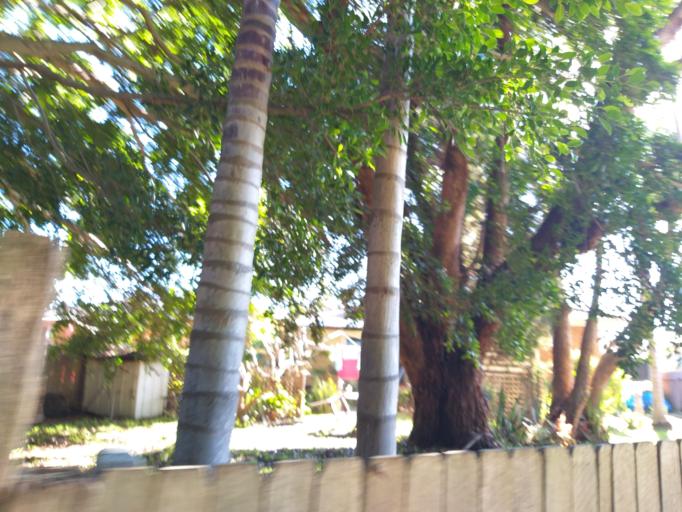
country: AU
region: New South Wales
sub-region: Wollongong
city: East Corrimal
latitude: -34.3705
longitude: 150.9230
